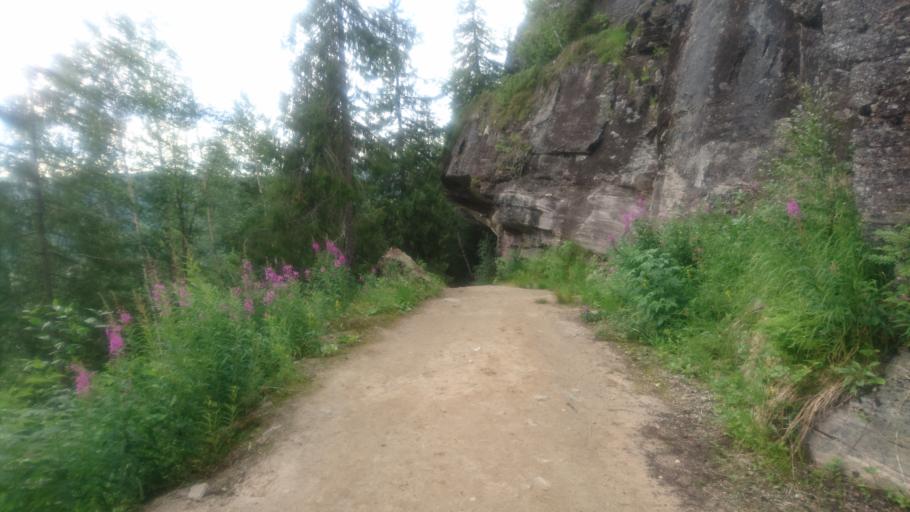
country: NO
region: Nordland
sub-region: Rana
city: Mo i Rana
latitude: 66.4153
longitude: 14.2627
